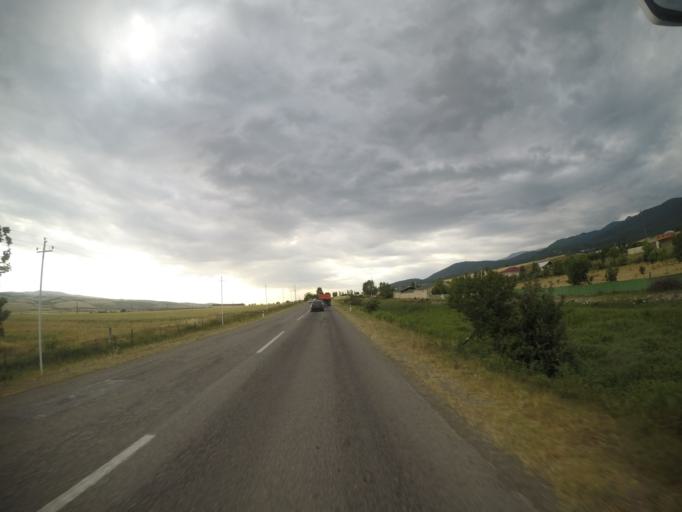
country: AZ
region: Ismayilli
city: Ismayilli
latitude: 40.7406
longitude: 48.2585
